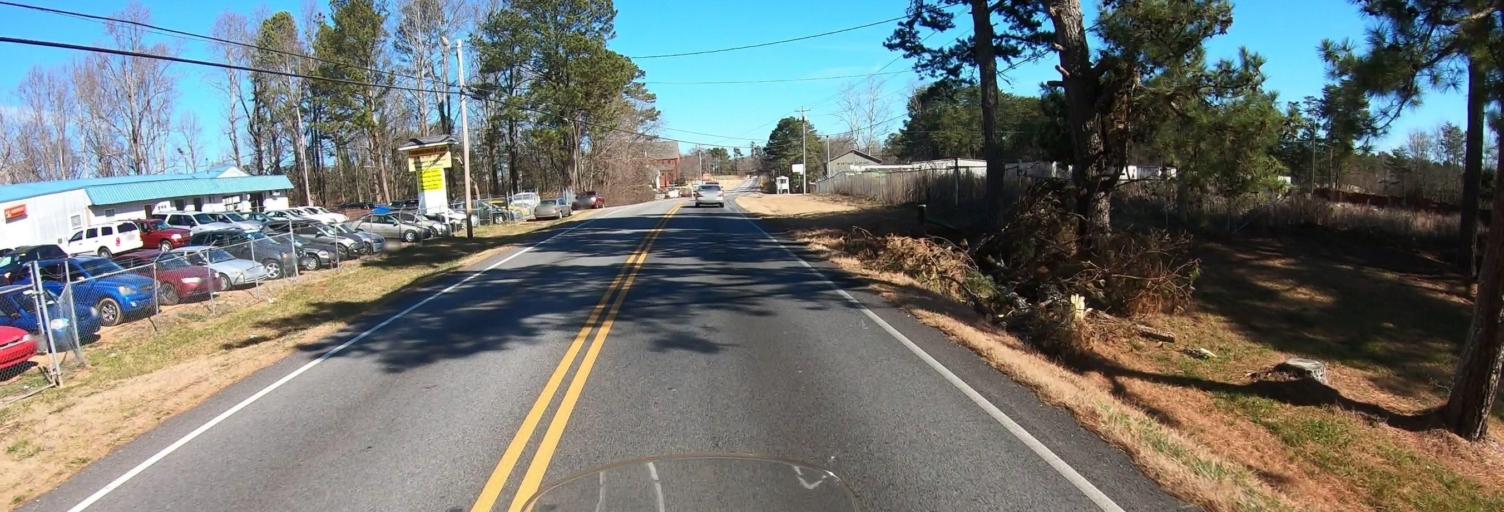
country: US
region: Georgia
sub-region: Hall County
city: Oakwood
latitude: 34.2782
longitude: -83.9031
